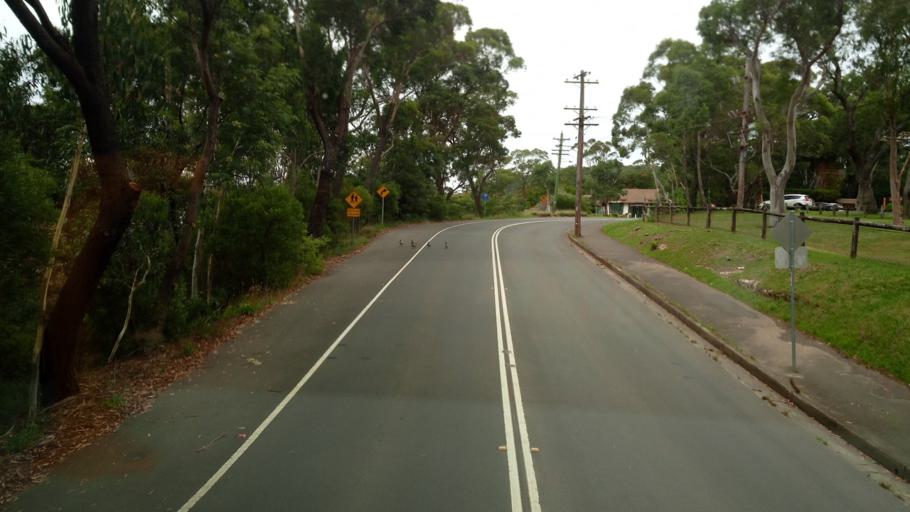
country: AU
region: New South Wales
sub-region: Blue Mountains Municipality
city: Katoomba
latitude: -33.7258
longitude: 150.3051
